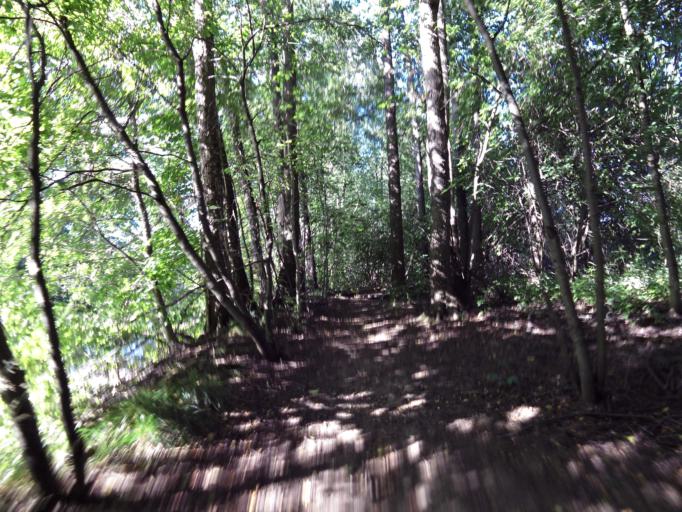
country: SE
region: Gaevleborg
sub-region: Gavle Kommun
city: Gavle
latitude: 60.7052
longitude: 17.1550
